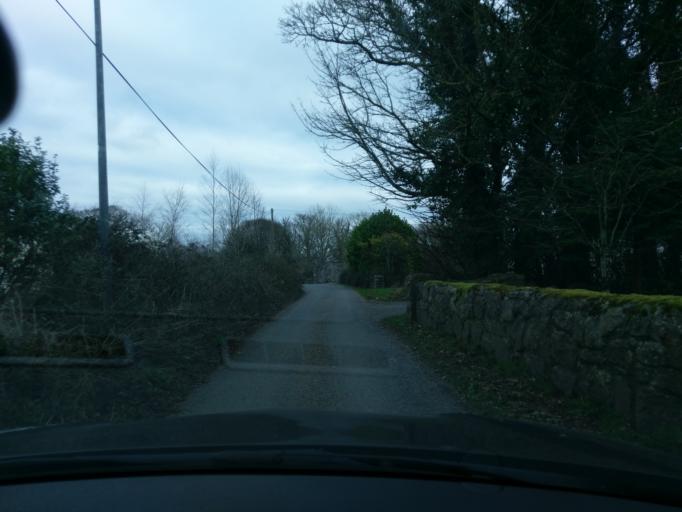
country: IE
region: Connaught
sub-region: County Galway
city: Oranmore
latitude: 53.2110
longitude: -8.8679
